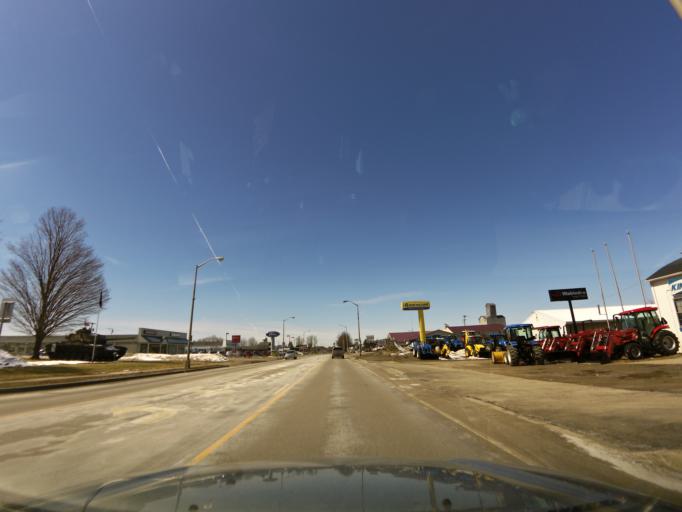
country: US
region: New York
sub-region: Wyoming County
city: Arcade
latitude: 42.5337
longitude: -78.4364
